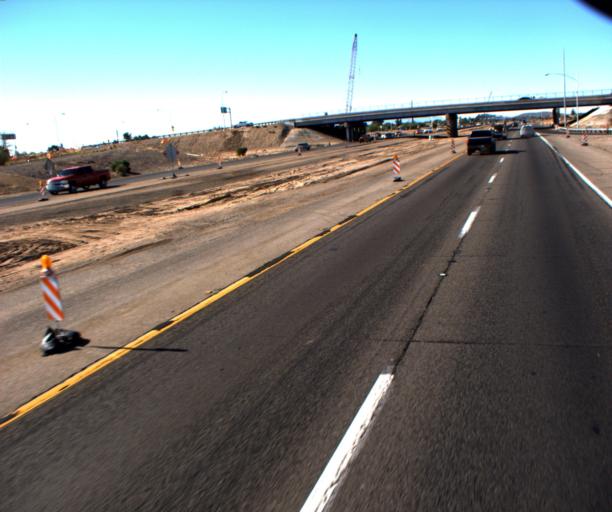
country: US
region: Arizona
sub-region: Pima County
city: South Tucson
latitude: 32.1793
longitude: -110.9858
